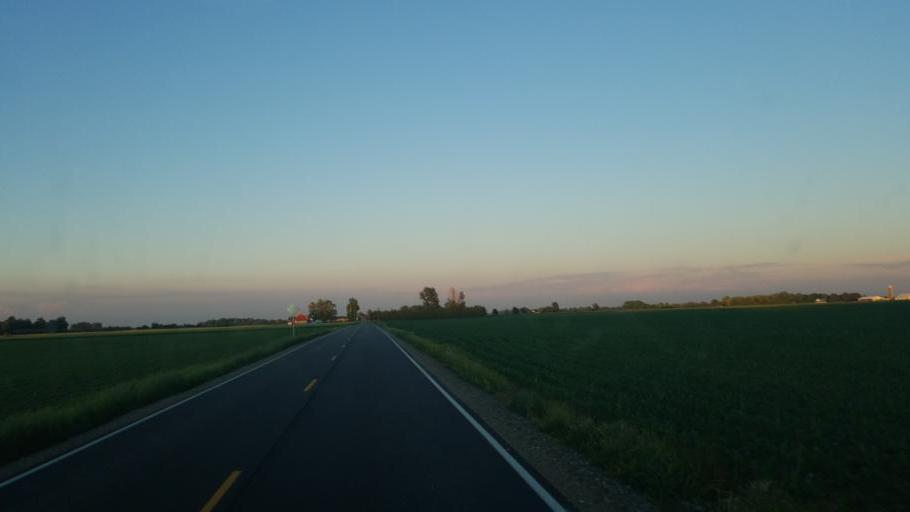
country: US
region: Indiana
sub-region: Elkhart County
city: Nappanee
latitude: 41.3613
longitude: -85.9986
